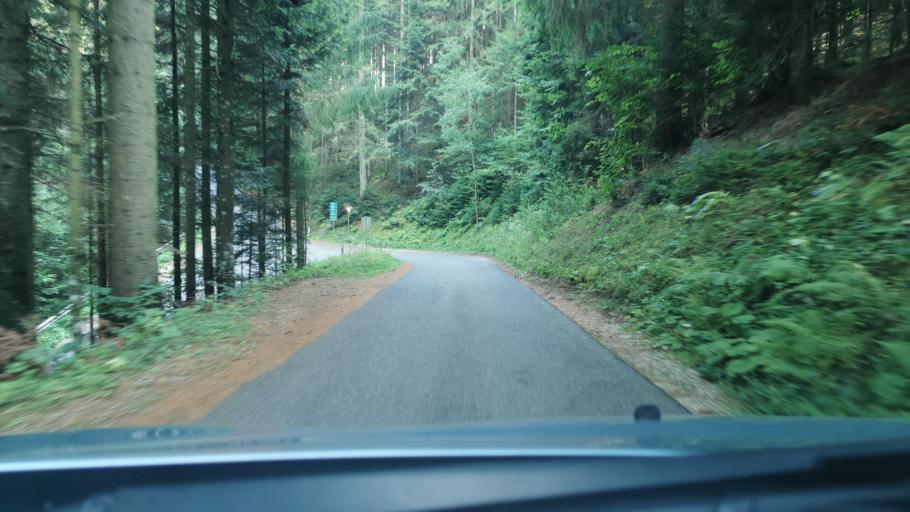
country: AT
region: Styria
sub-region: Politischer Bezirk Weiz
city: Strallegg
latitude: 47.4005
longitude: 15.6980
